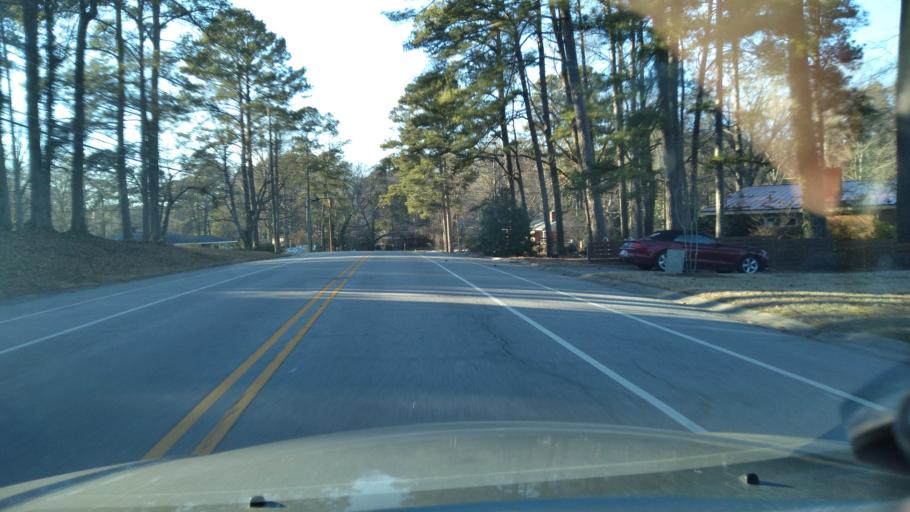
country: US
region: North Carolina
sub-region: Wake County
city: Garner
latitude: 35.7004
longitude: -78.6237
